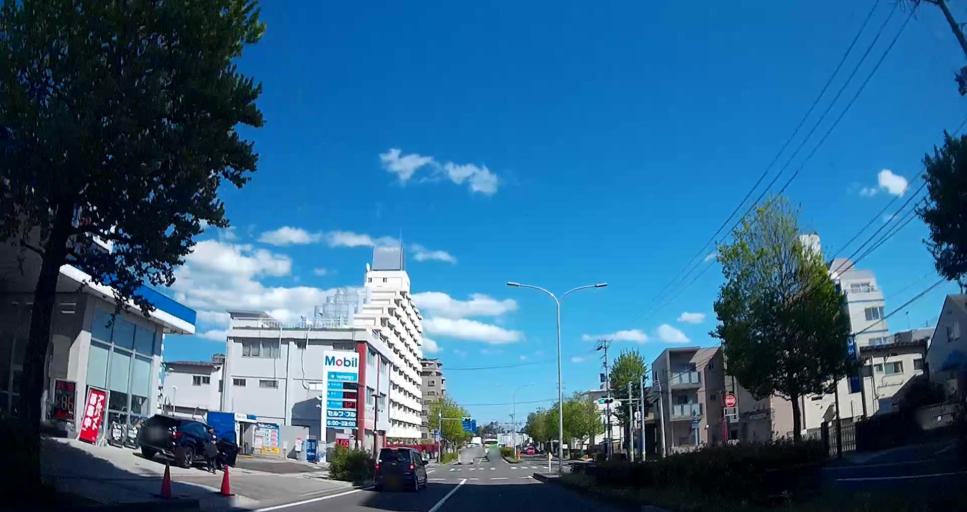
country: JP
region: Miyagi
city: Sendai-shi
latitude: 38.2548
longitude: 140.8964
